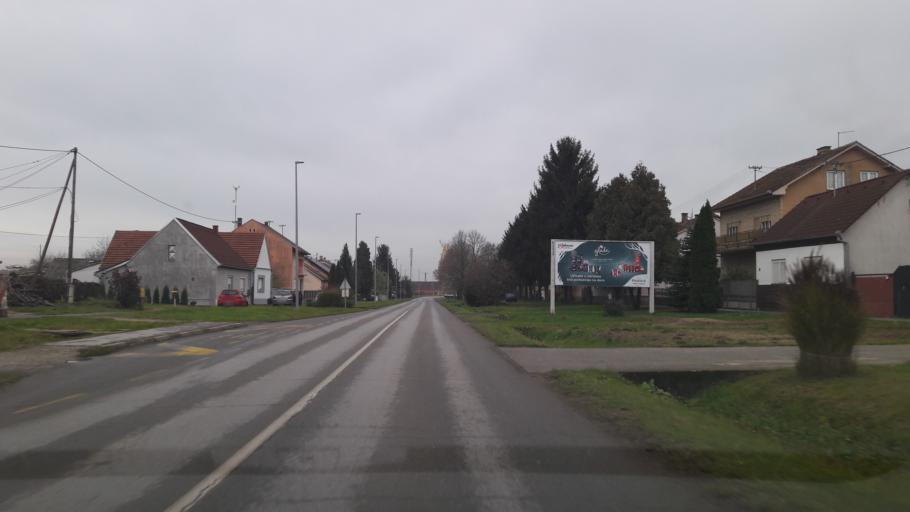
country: HR
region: Osjecko-Baranjska
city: Josipovac
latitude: 45.5815
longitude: 18.5836
